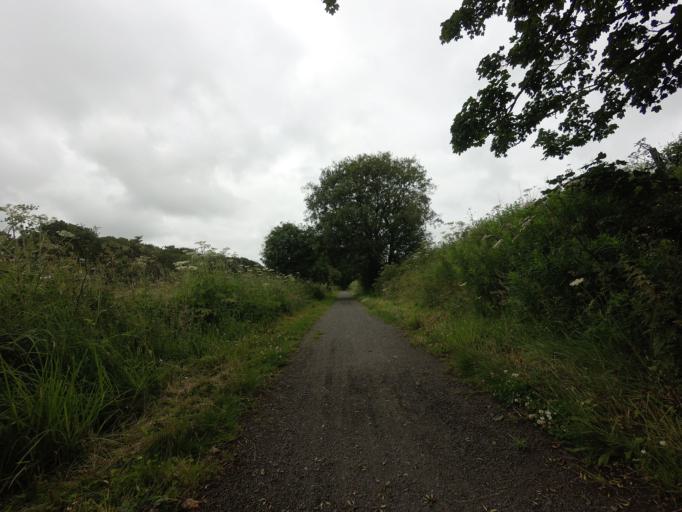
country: GB
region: Scotland
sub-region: Aberdeenshire
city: Mintlaw
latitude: 57.5142
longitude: -2.1373
